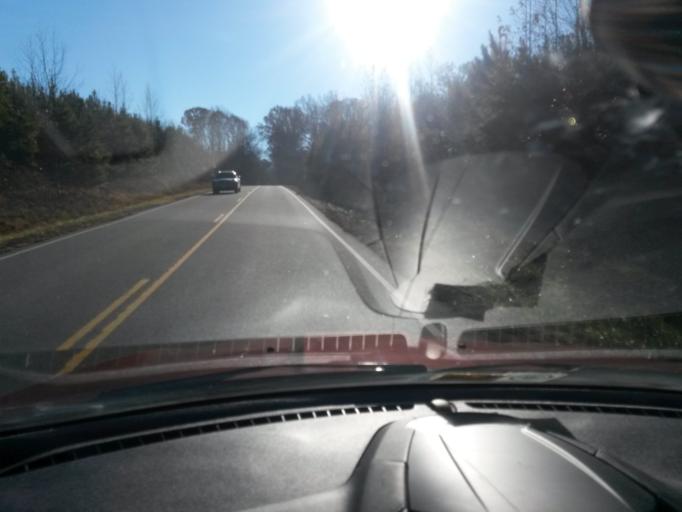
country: US
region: Virginia
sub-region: Charlotte County
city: Charlotte Court House
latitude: 37.1228
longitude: -78.6555
